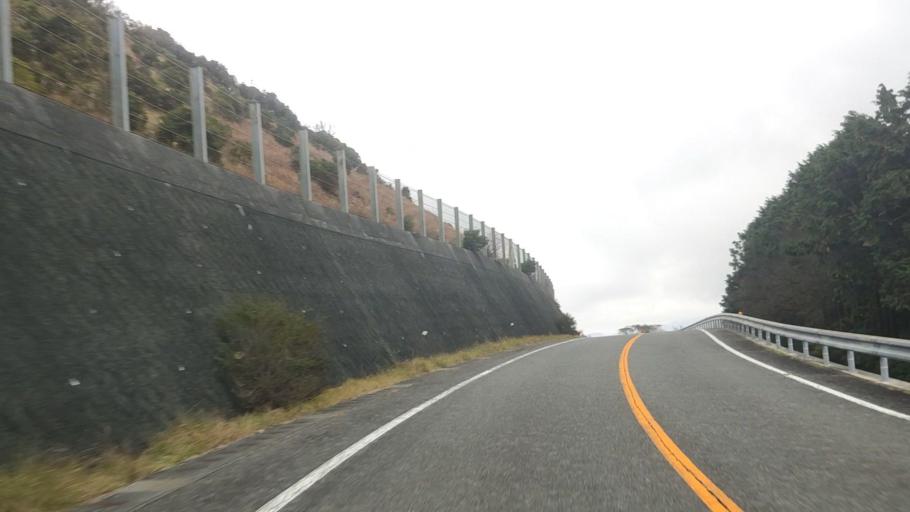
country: JP
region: Shizuoka
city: Heda
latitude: 34.8812
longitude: 138.8417
